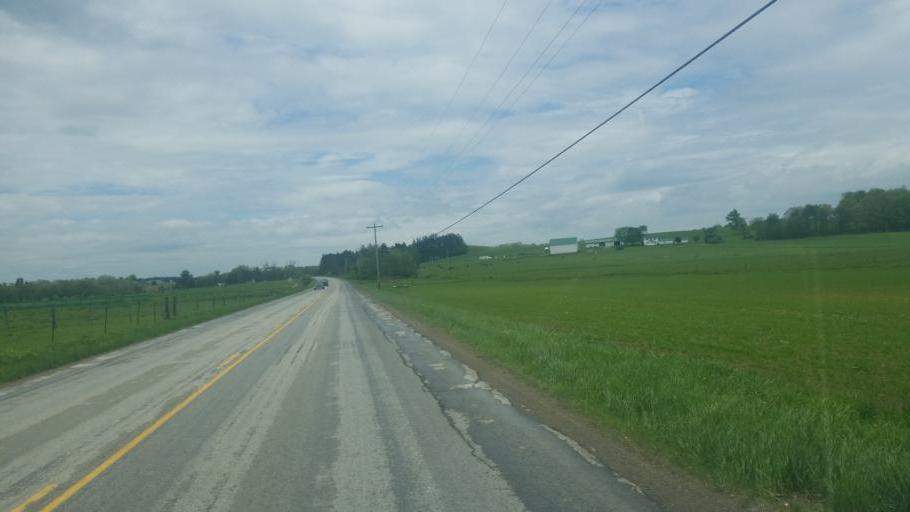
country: US
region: Pennsylvania
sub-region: Clarion County
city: Marianne
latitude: 41.3755
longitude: -79.3902
